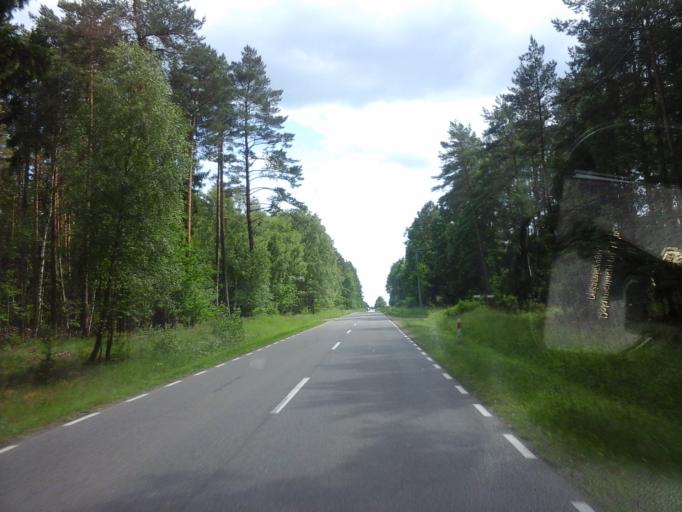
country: PL
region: West Pomeranian Voivodeship
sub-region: Powiat swidwinski
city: Slawoborze
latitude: 53.8692
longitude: 15.7291
